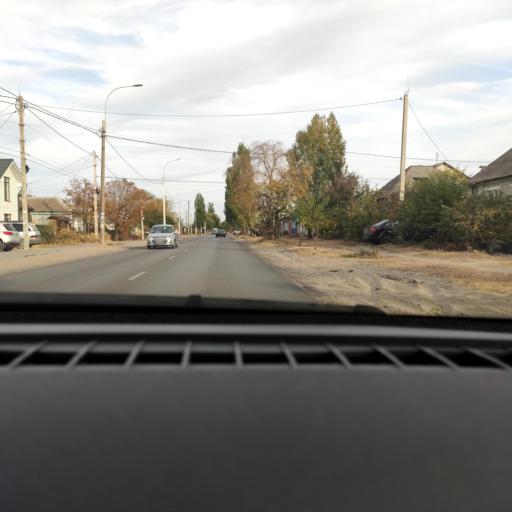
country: RU
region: Voronezj
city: Somovo
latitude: 51.7390
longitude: 39.2821
